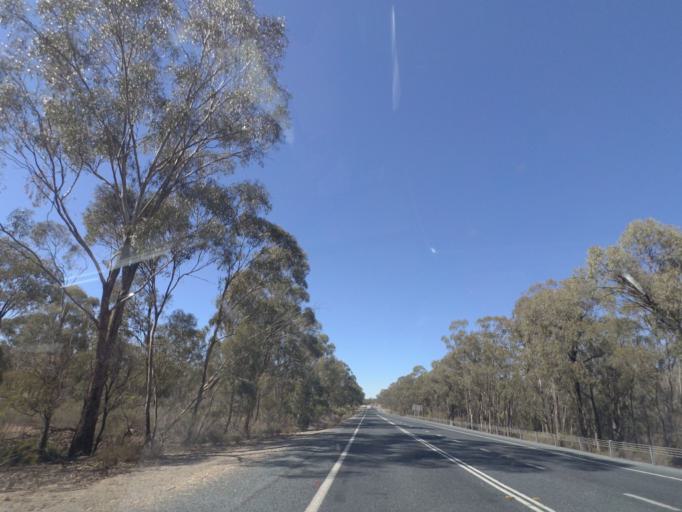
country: AU
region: New South Wales
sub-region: Bland
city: West Wyalong
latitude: -34.1340
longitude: 147.1224
